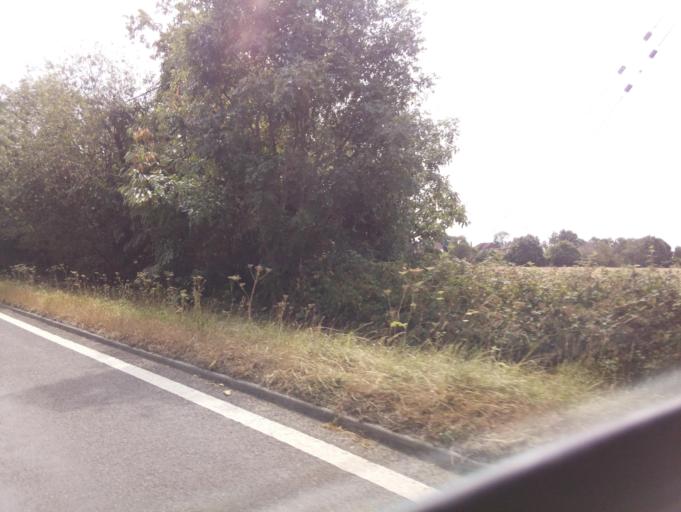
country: GB
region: England
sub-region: Surrey
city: Headley
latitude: 51.2446
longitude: -0.2568
